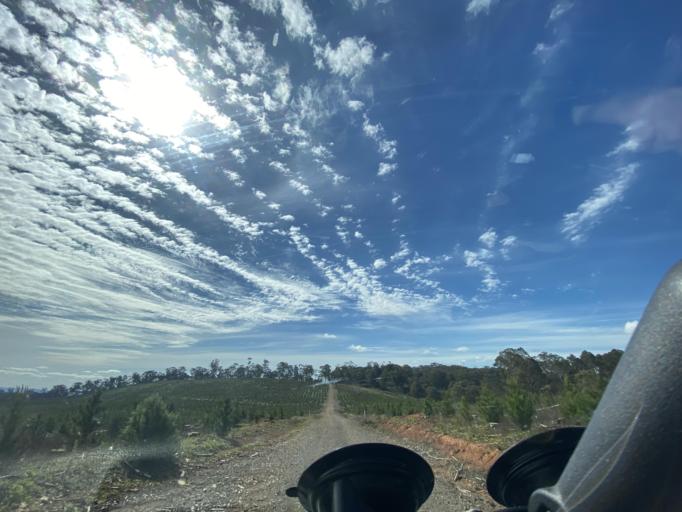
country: AU
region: Victoria
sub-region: Mansfield
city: Mansfield
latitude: -36.8216
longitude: 146.1029
